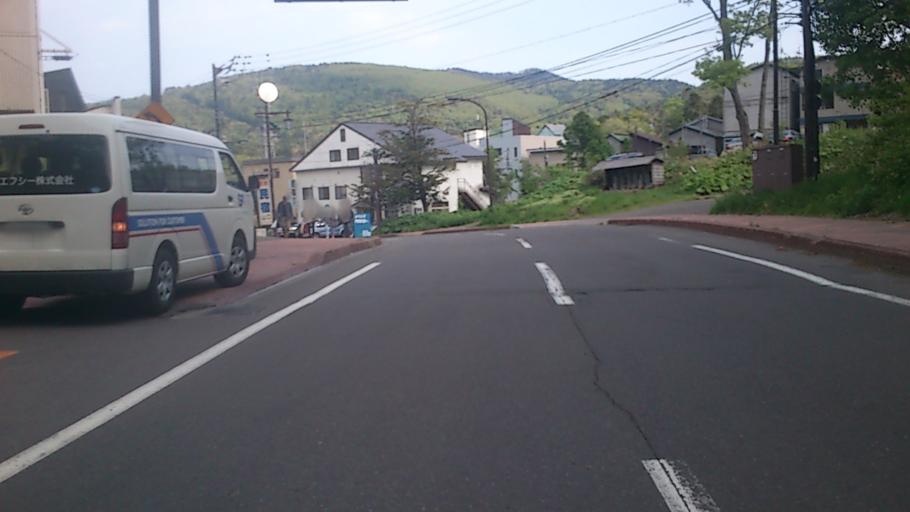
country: JP
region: Hokkaido
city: Bihoro
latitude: 43.4350
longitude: 144.0893
